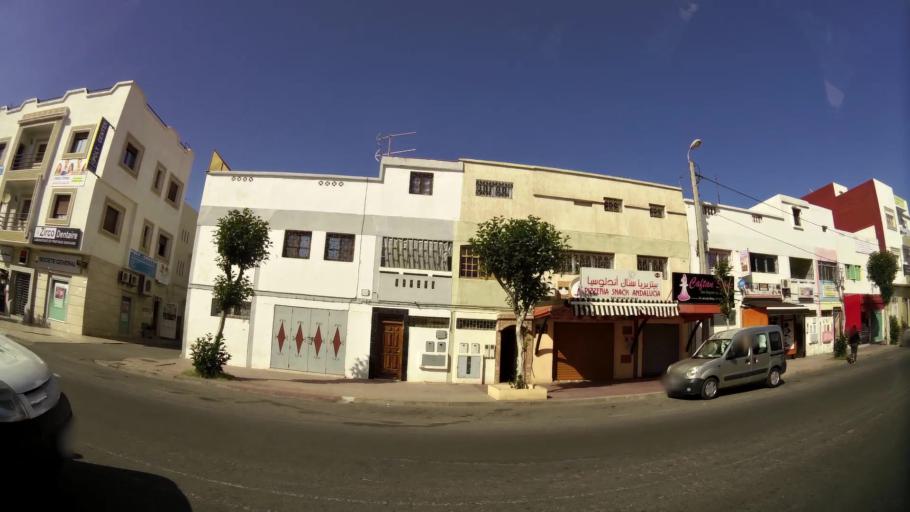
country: MA
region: Oued ed Dahab-Lagouira
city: Dakhla
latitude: 30.4233
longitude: -9.5626
